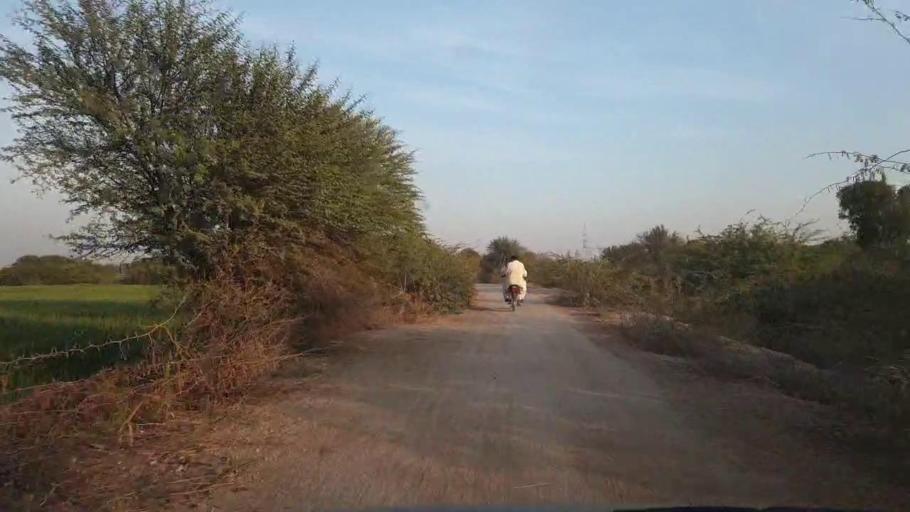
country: PK
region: Sindh
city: Chambar
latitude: 25.2849
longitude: 68.8198
